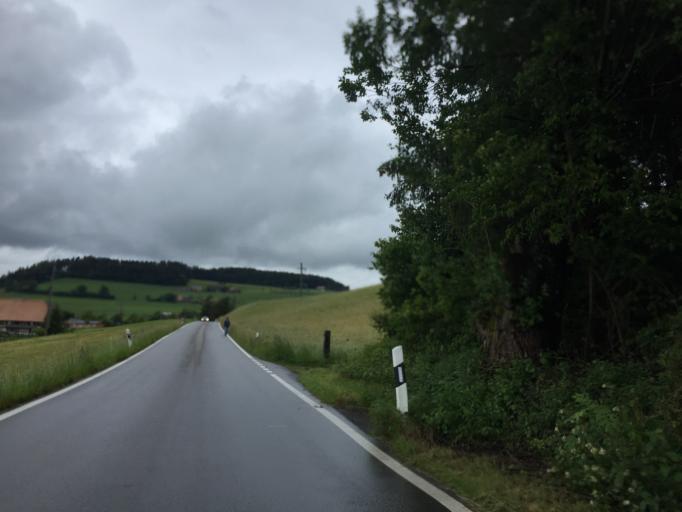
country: CH
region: Bern
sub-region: Bern-Mittelland District
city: Biglen
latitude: 46.9087
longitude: 7.6277
